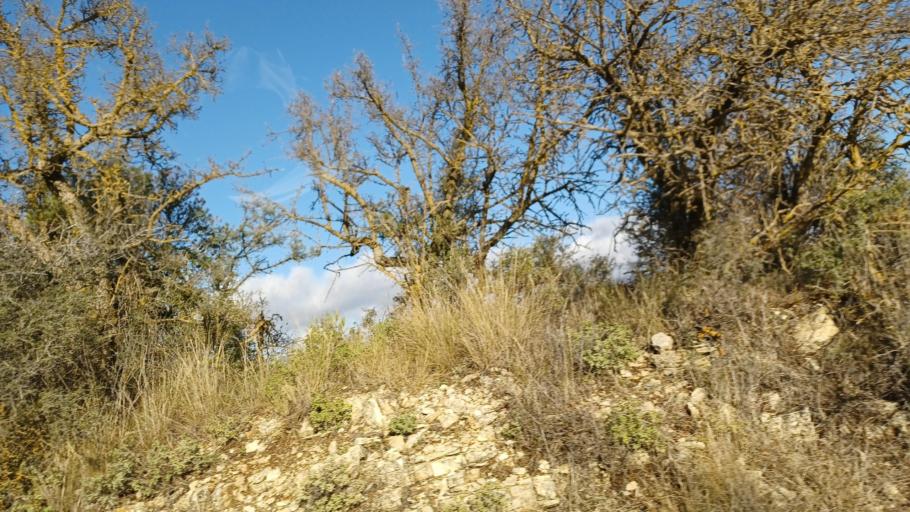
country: CY
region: Limassol
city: Pachna
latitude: 34.8418
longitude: 32.6821
